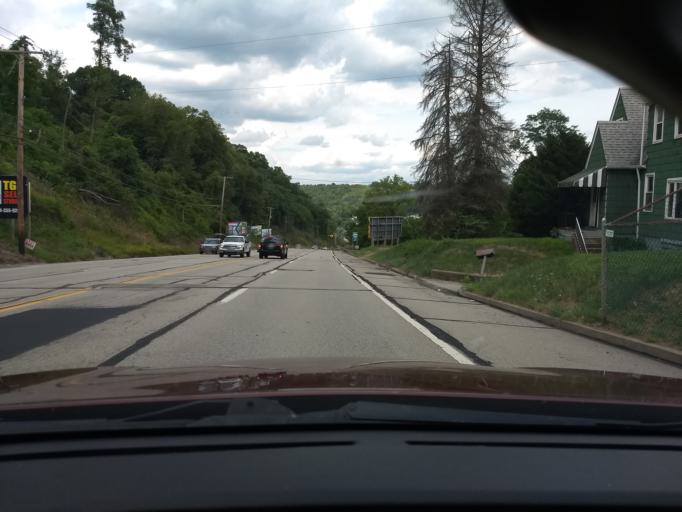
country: US
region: Pennsylvania
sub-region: Armstrong County
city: Freeport
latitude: 40.6705
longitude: -79.6977
